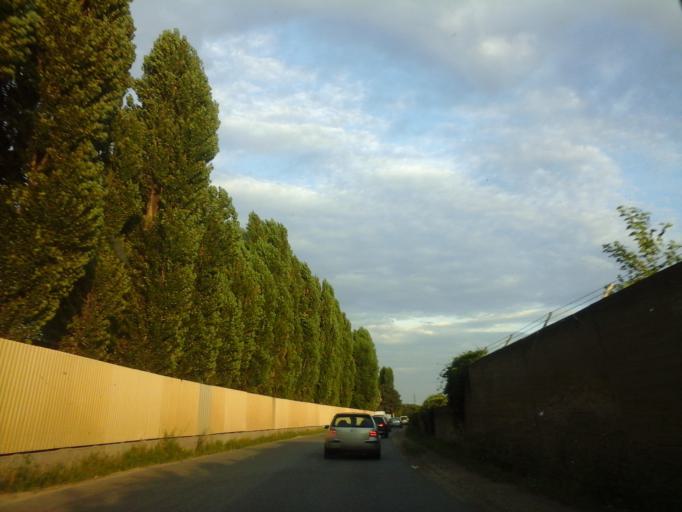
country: AT
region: Lower Austria
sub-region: Politischer Bezirk Wien-Umgebung
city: Schwechat
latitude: 48.1743
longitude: 16.4690
